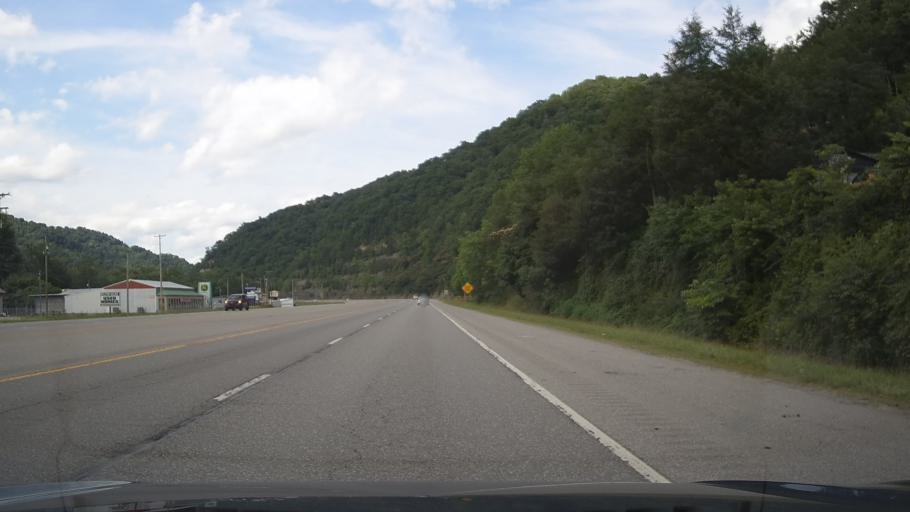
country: US
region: Kentucky
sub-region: Pike County
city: Coal Run Village
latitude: 37.5821
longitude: -82.6600
